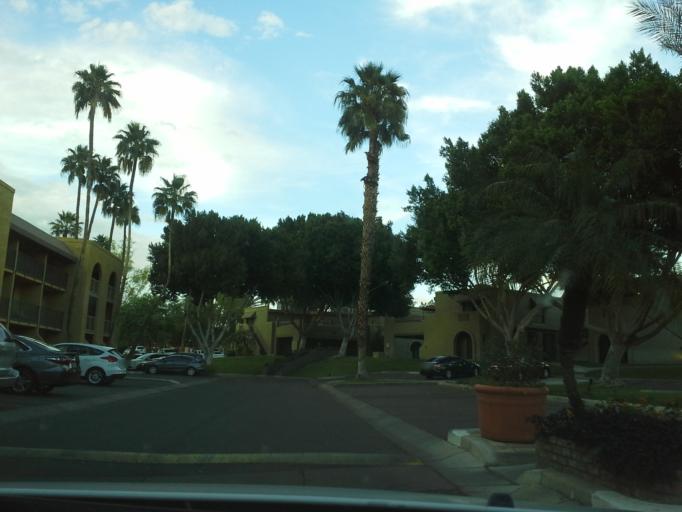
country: US
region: Arizona
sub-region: Maricopa County
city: Phoenix
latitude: 33.5476
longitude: -112.0449
